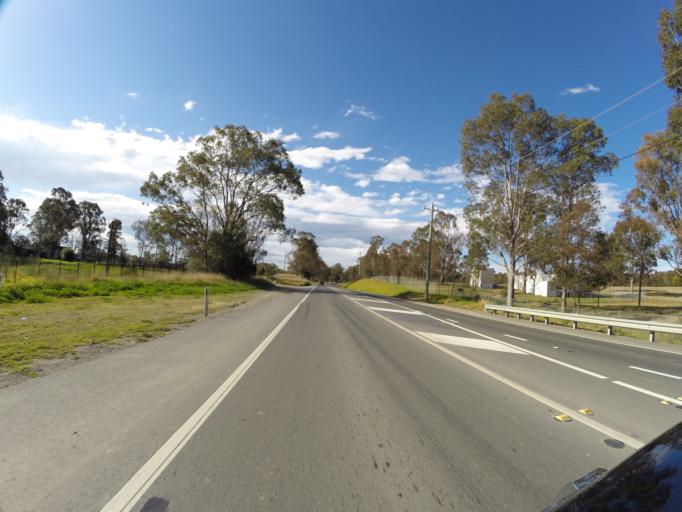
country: AU
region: New South Wales
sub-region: Fairfield
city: Cecil Park
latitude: -33.8769
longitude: 150.8266
